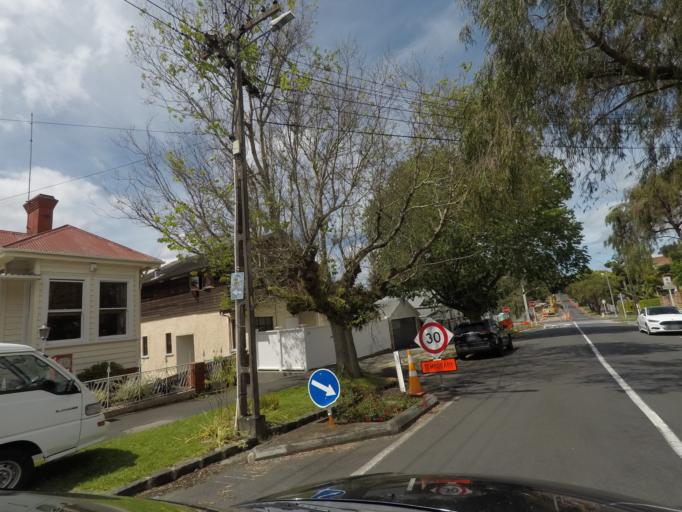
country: NZ
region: Auckland
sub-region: Auckland
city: Auckland
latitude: -36.8410
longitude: 174.7389
